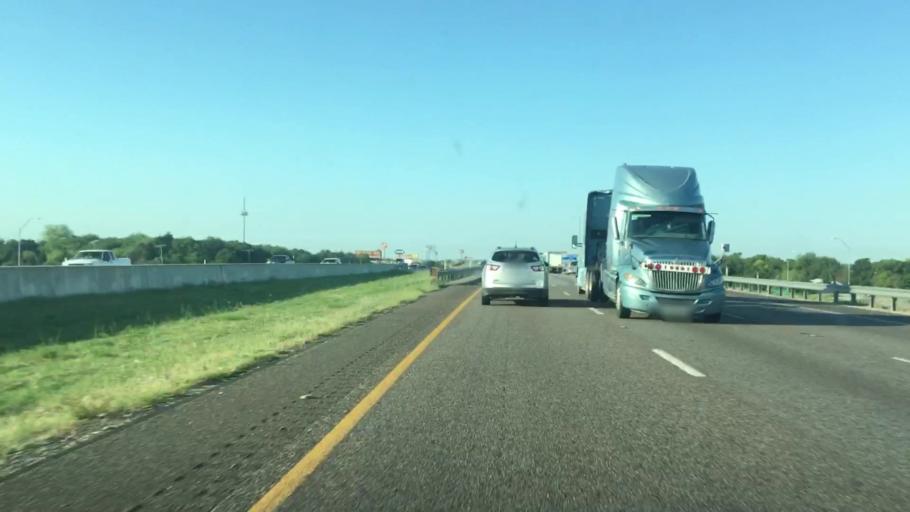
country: US
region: Texas
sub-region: McLennan County
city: Lacy-Lakeview
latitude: 31.6156
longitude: -97.1015
